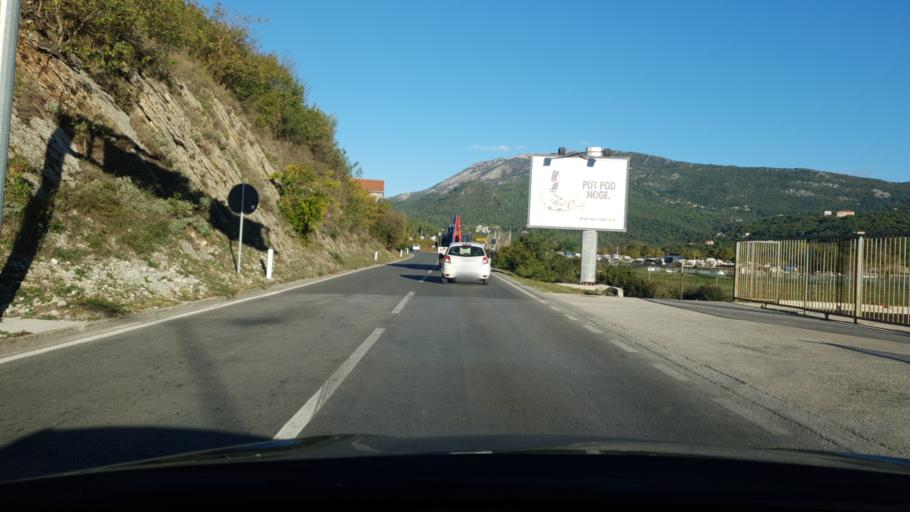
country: ME
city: Igalo
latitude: 42.4577
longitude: 18.4915
